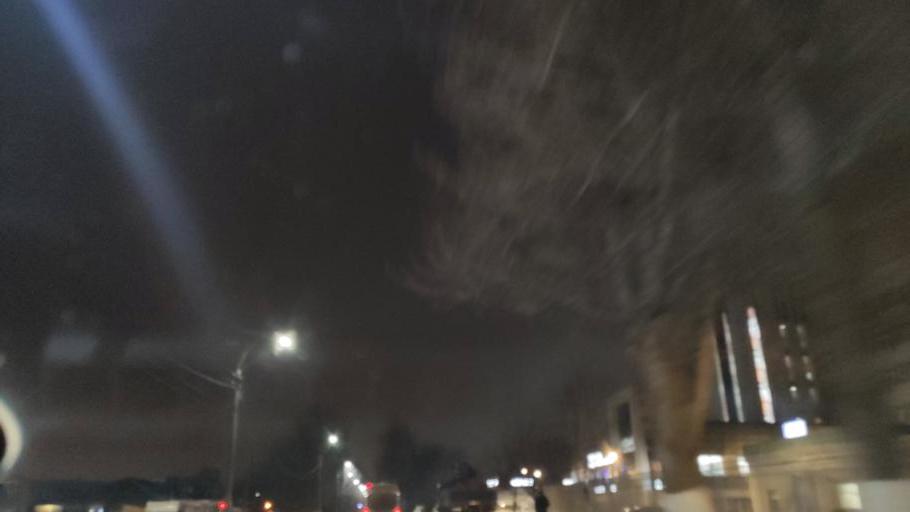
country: RU
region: Moskovskaya
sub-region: Podol'skiy Rayon
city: Podol'sk
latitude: 55.4384
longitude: 37.5728
